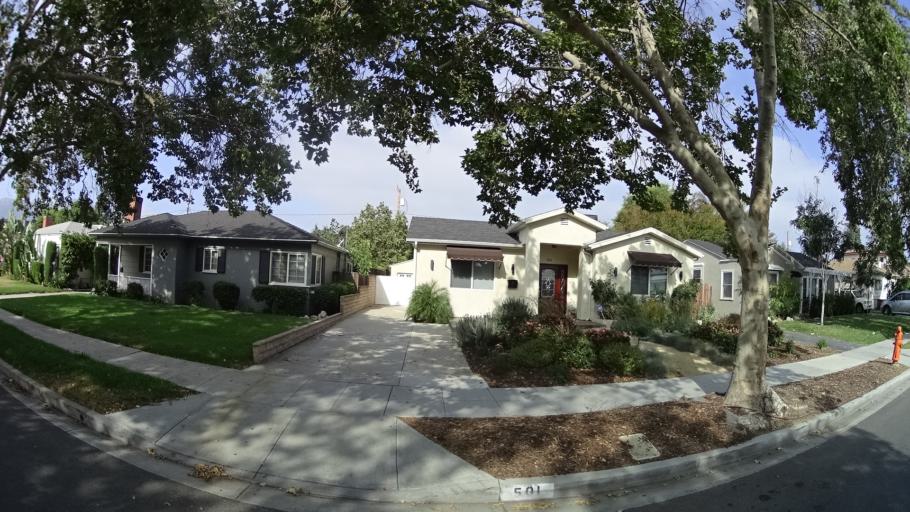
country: US
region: California
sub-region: Los Angeles County
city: Burbank
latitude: 34.1639
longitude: -118.3167
